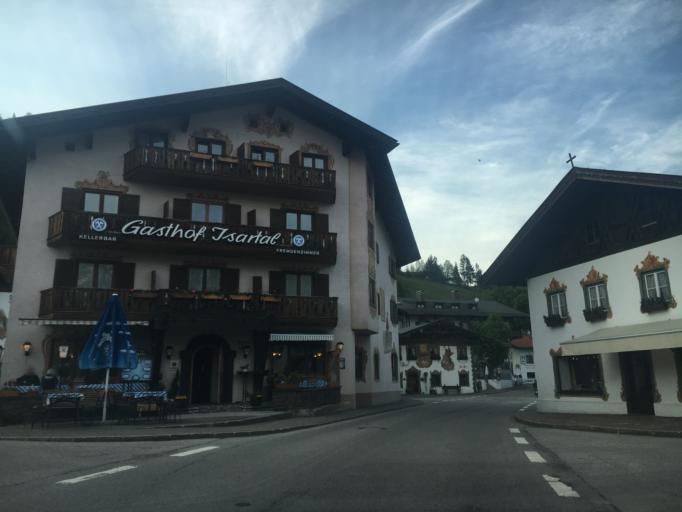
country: DE
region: Bavaria
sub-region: Upper Bavaria
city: Wallgau
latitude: 47.5211
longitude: 11.2817
